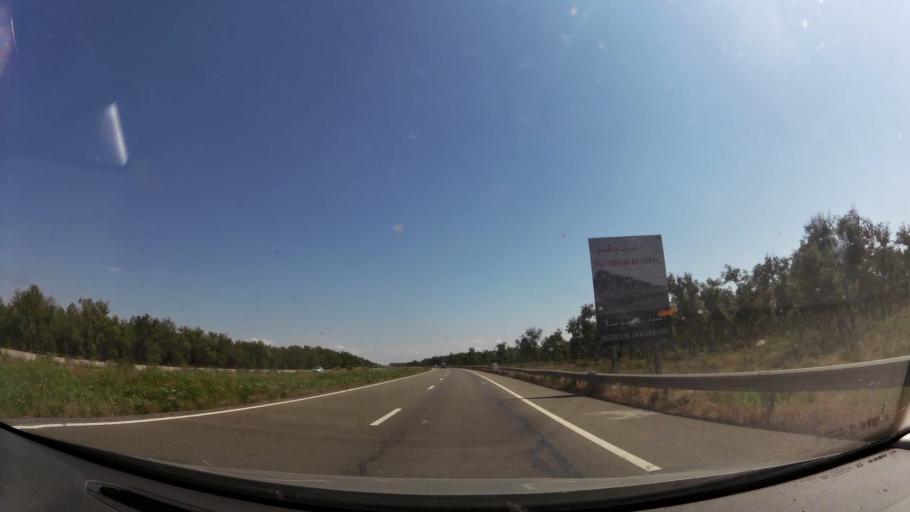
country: MA
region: Rabat-Sale-Zemmour-Zaer
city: Sale
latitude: 34.0626
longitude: -6.7117
